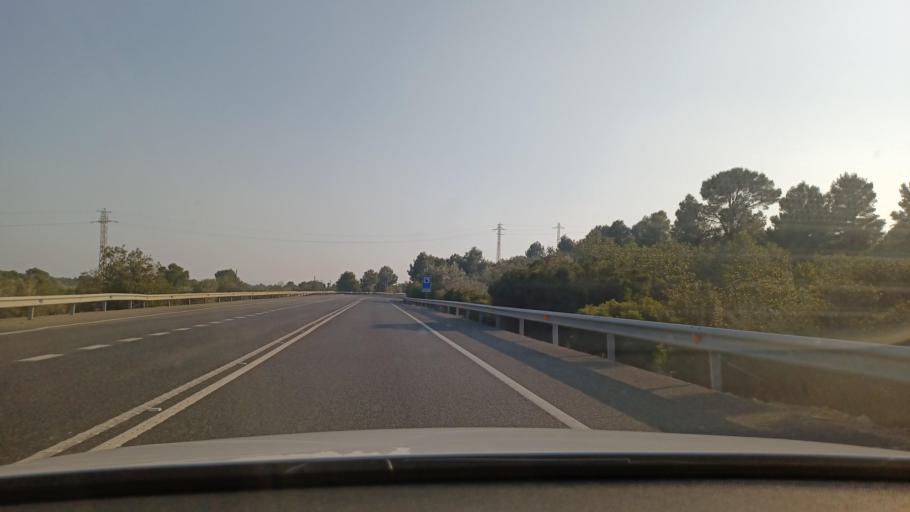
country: ES
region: Catalonia
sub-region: Provincia de Tarragona
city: L'Ampolla
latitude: 40.8428
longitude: 0.7101
